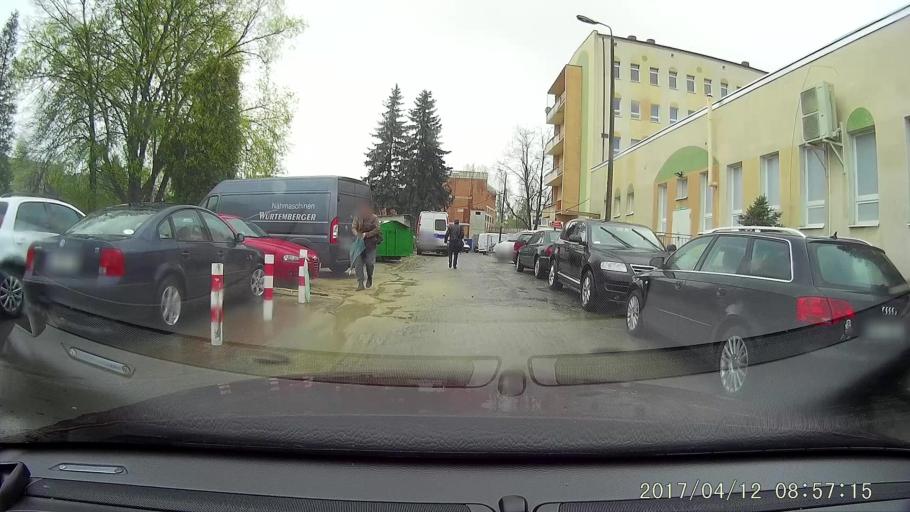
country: PL
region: Lower Silesian Voivodeship
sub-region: Powiat zgorzelecki
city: Zgorzelec
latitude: 51.1582
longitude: 15.0119
